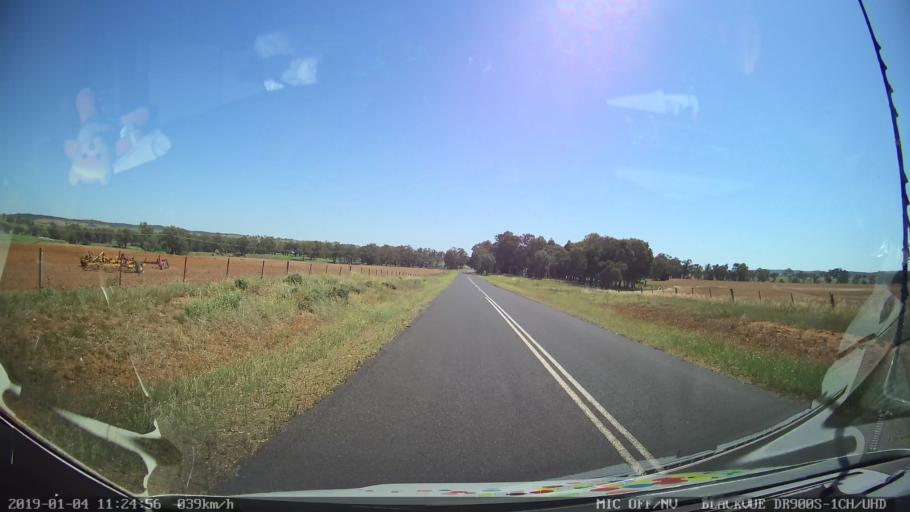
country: AU
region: New South Wales
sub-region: Cabonne
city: Molong
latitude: -33.1300
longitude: 148.7522
